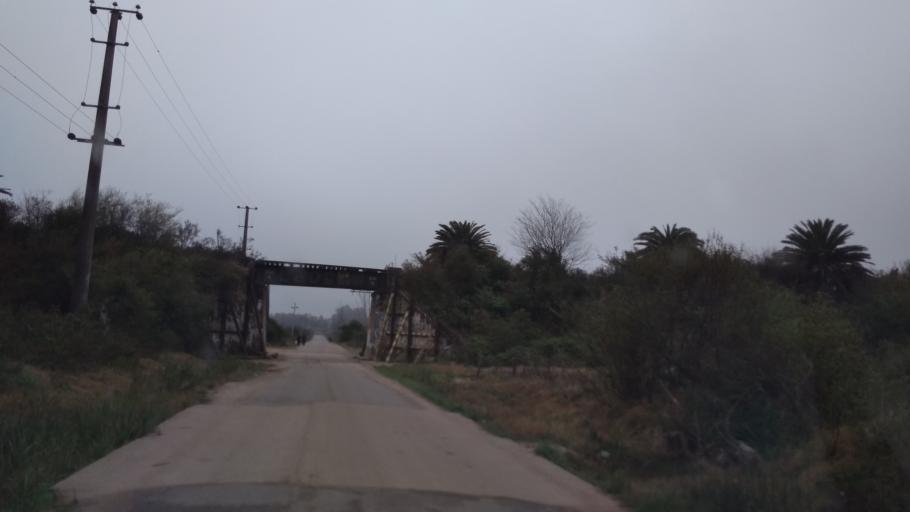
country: UY
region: Florida
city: Florida
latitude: -34.0868
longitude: -56.2071
